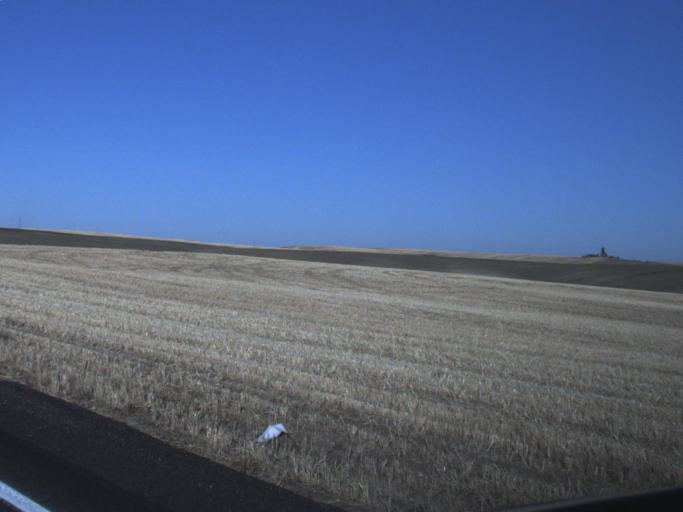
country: US
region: Washington
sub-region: Adams County
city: Ritzville
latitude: 47.0224
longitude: -118.3494
